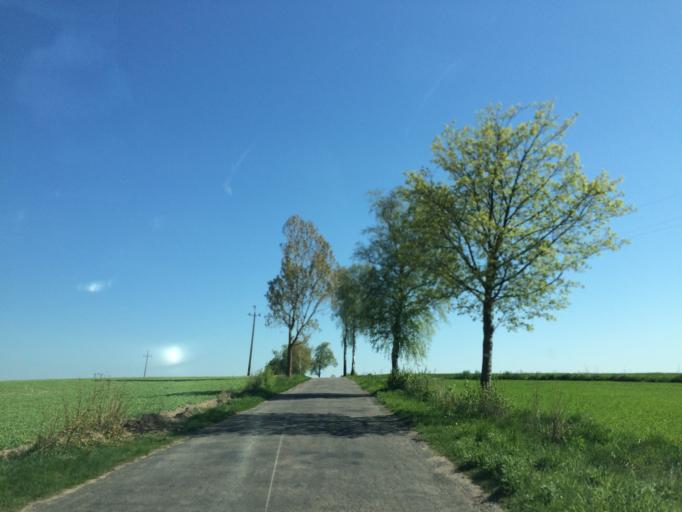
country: PL
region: Warmian-Masurian Voivodeship
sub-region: Powiat nowomiejski
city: Kurzetnik
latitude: 53.4704
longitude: 19.4789
